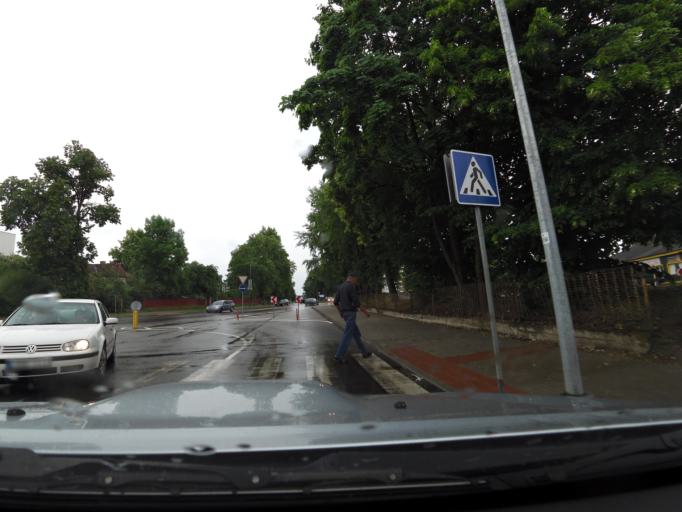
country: LT
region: Marijampoles apskritis
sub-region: Marijampole Municipality
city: Marijampole
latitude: 54.5475
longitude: 23.3471
